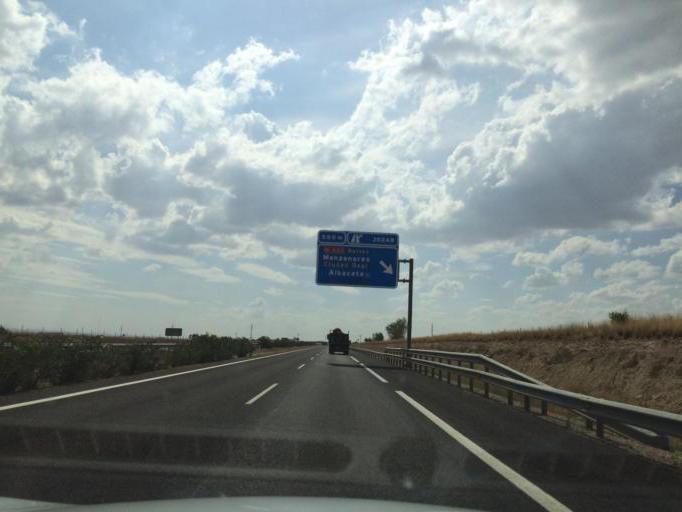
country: ES
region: Castille-La Mancha
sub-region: Provincia de Albacete
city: Albacete
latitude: 39.0059
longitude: -1.8922
